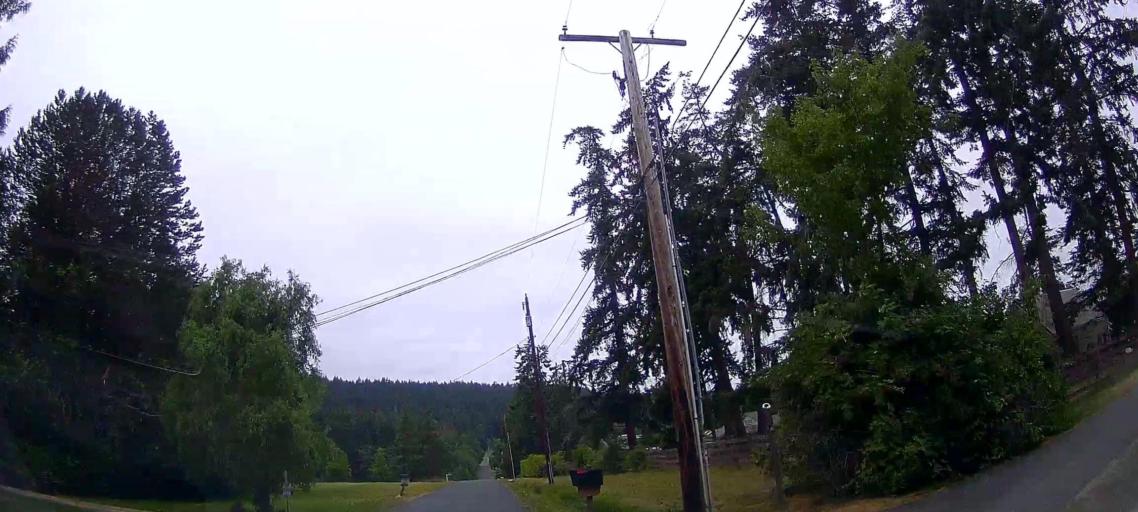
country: US
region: Washington
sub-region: Skagit County
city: Anacortes
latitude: 48.4336
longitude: -122.6128
